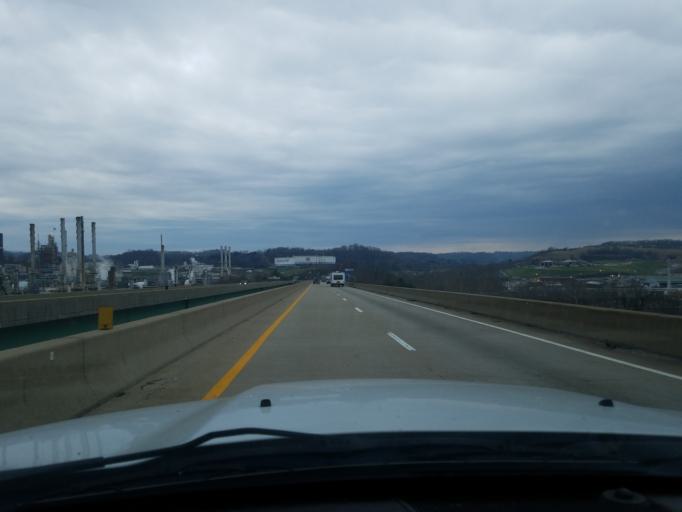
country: US
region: West Virginia
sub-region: Wayne County
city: Kenova
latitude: 38.3819
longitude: -82.5928
